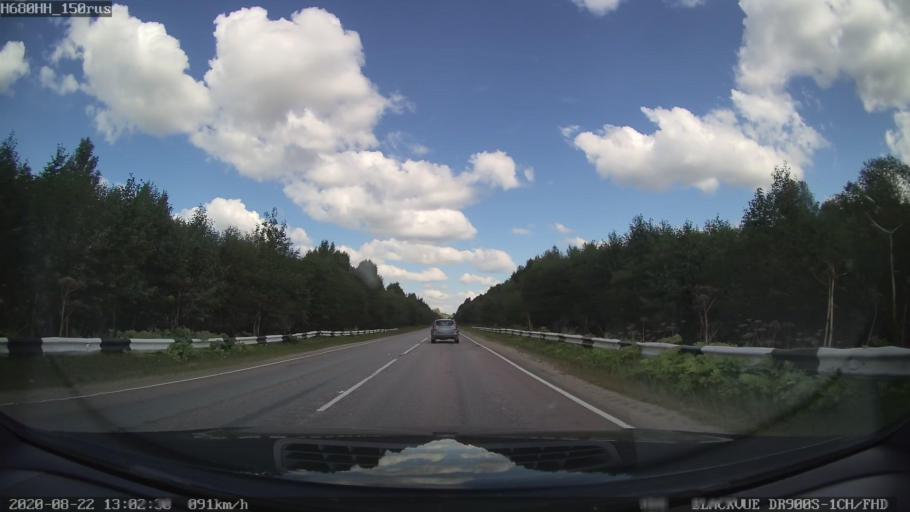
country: RU
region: Tverskaya
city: Bezhetsk
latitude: 57.6498
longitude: 36.3980
